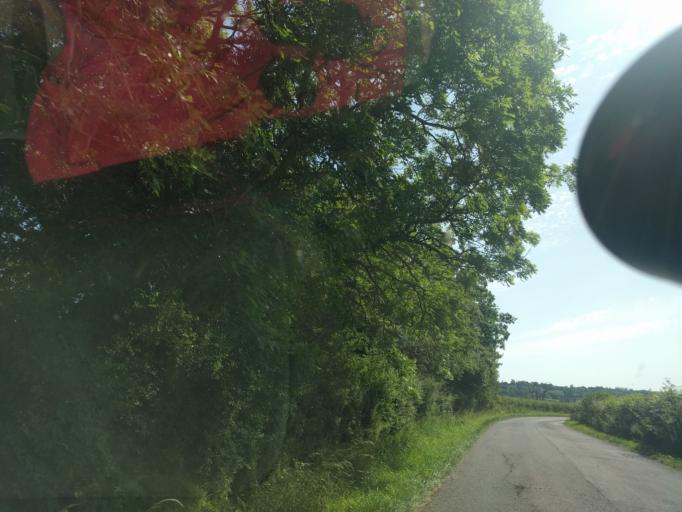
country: GB
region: England
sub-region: Wiltshire
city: Lyneham
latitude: 51.5408
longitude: -1.9760
